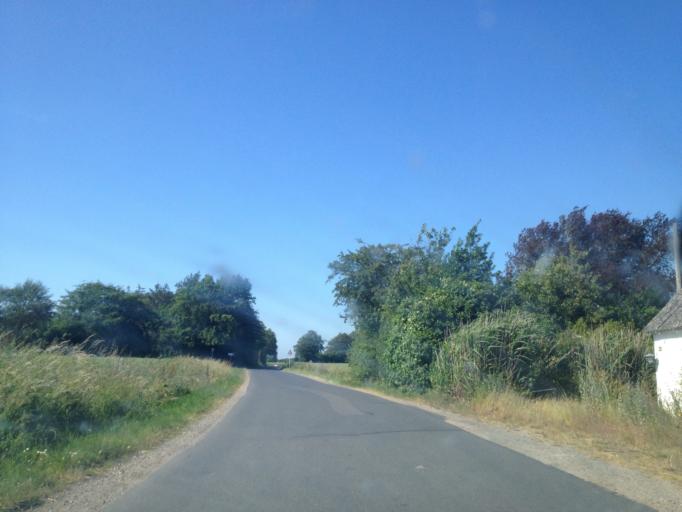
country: DK
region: South Denmark
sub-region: Kolding Kommune
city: Christiansfeld
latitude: 55.4017
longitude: 9.5175
